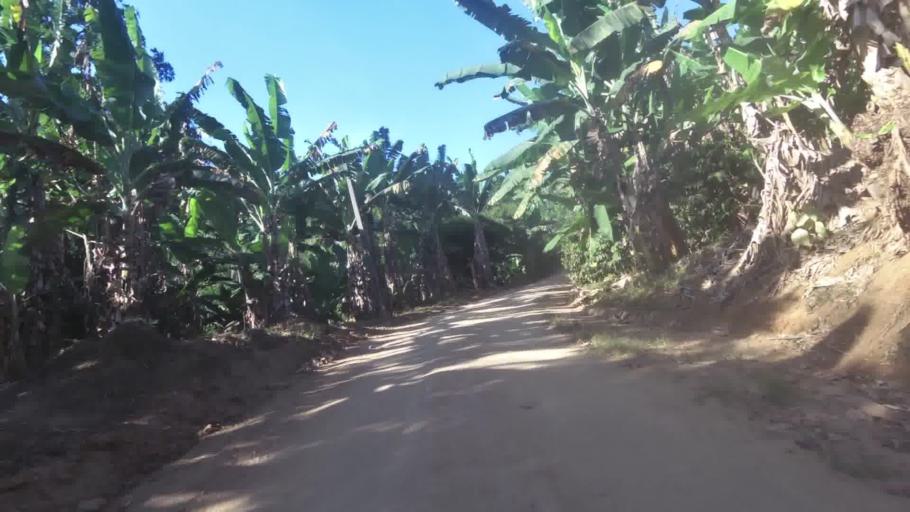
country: BR
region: Espirito Santo
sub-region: Iconha
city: Iconha
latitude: -20.7592
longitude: -40.8198
